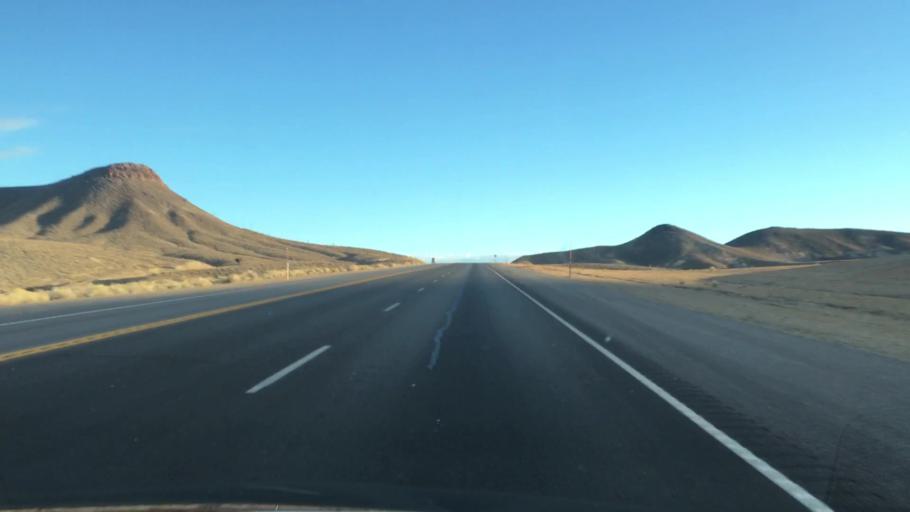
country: US
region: Nevada
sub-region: Esmeralda County
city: Goldfield
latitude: 37.6860
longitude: -117.2320
